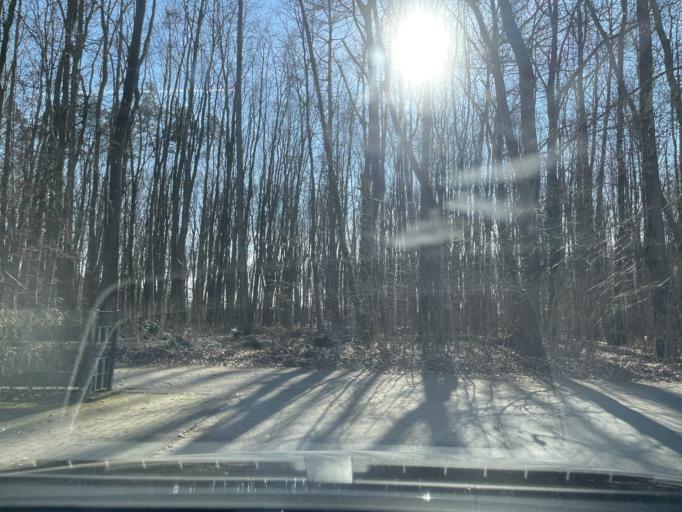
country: DE
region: North Rhine-Westphalia
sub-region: Regierungsbezirk Dusseldorf
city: Schwalmtal
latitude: 51.2017
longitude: 6.2955
